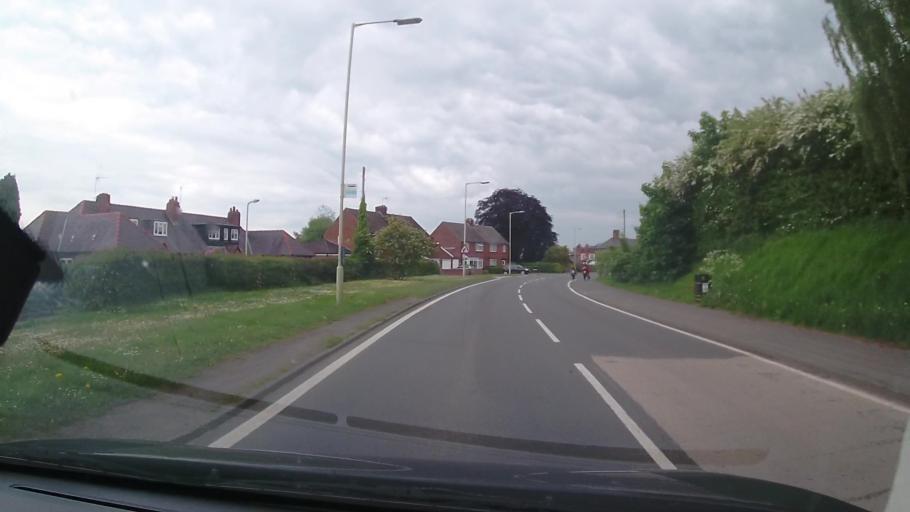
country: GB
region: England
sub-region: Shropshire
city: Ellesmere
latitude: 52.9053
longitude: -2.9024
